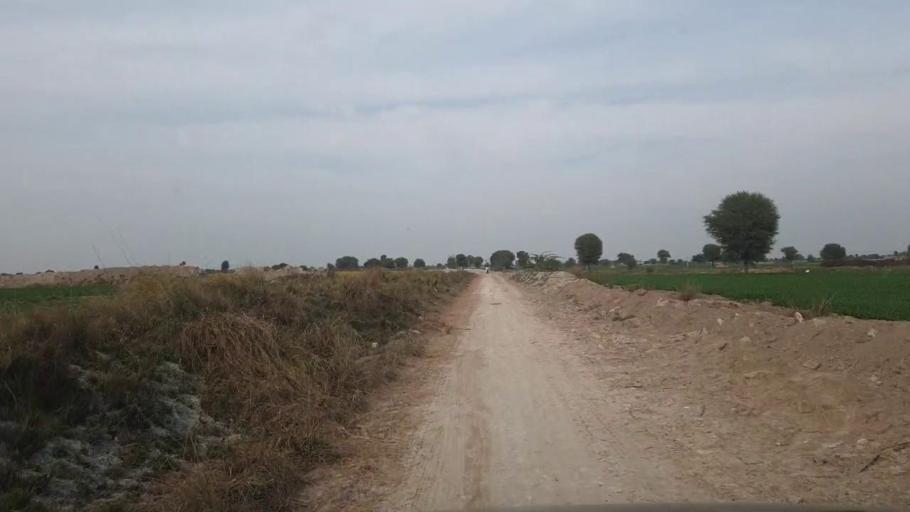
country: PK
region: Sindh
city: Shahpur Chakar
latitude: 26.1185
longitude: 68.5102
